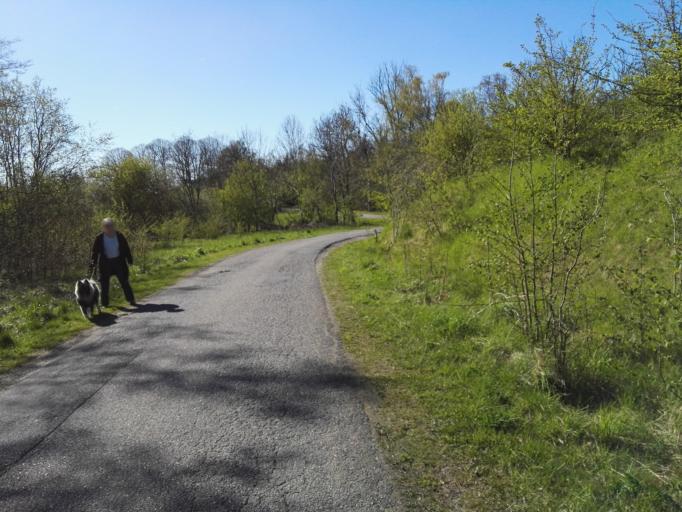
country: DK
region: Capital Region
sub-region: Egedal Kommune
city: Vekso
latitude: 55.7532
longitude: 12.2282
